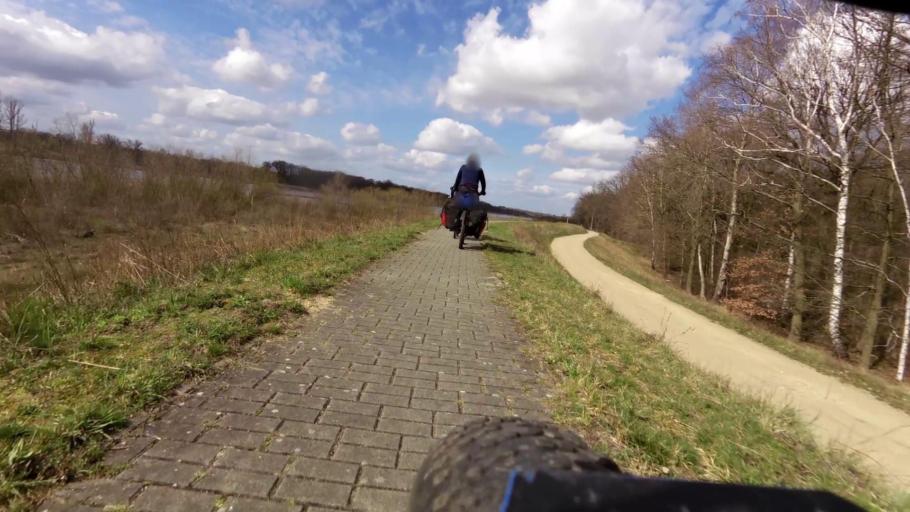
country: PL
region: Lubusz
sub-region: Powiat slubicki
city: Slubice
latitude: 52.3818
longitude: 14.5502
